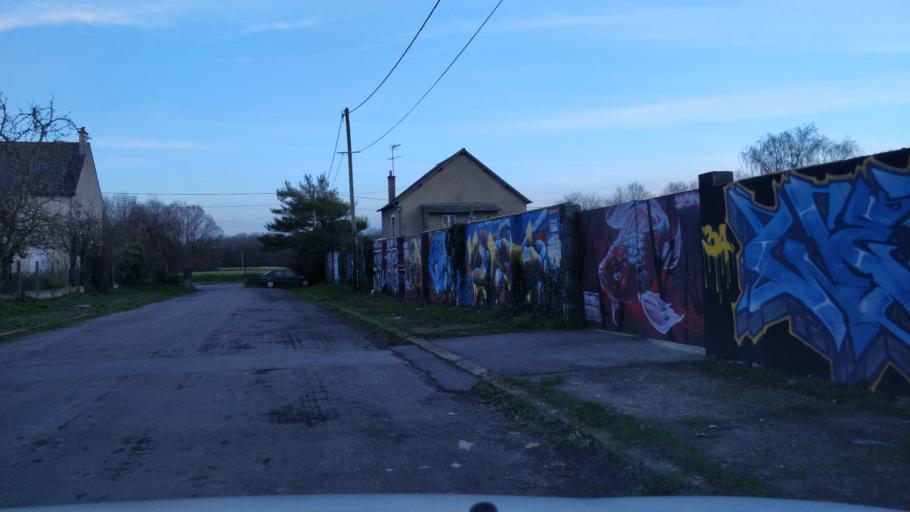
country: FR
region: Brittany
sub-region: Departement d'Ille-et-Vilaine
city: Saint-Jacques-de-la-Lande
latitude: 48.0995
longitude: -1.7254
